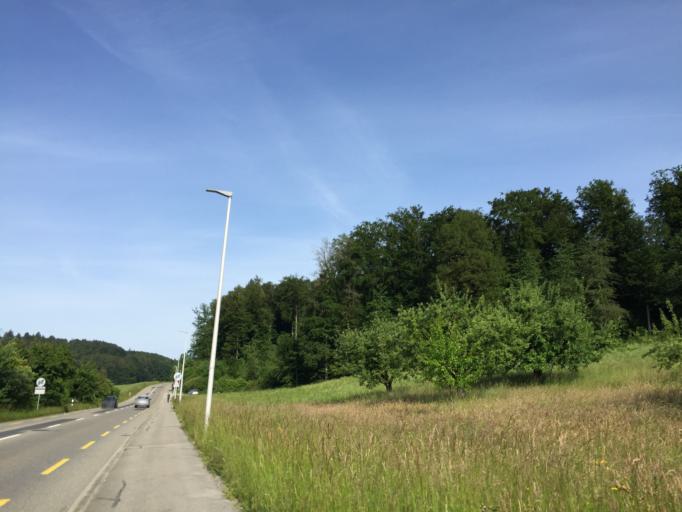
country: CH
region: Bern
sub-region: Bern-Mittelland District
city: Koniz
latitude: 46.9200
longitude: 7.4017
